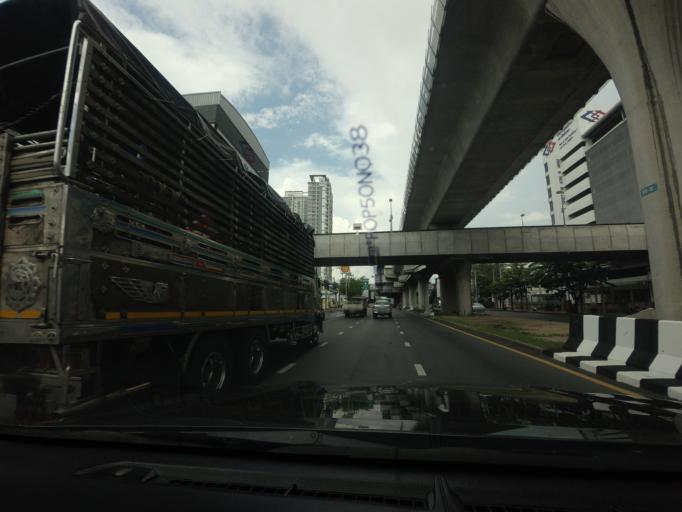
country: TH
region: Bangkok
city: Bang Khae
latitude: 13.7108
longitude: 100.4113
